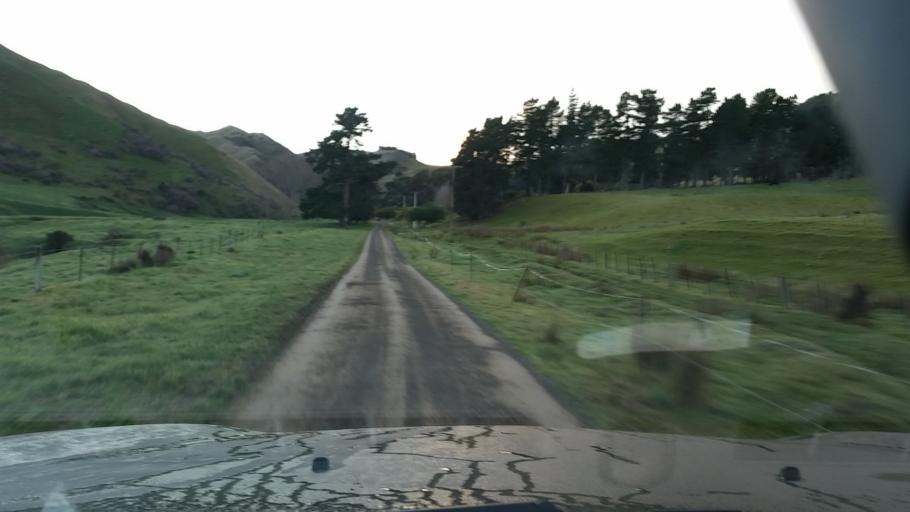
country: NZ
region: Marlborough
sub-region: Marlborough District
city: Blenheim
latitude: -41.5760
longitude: 173.9476
